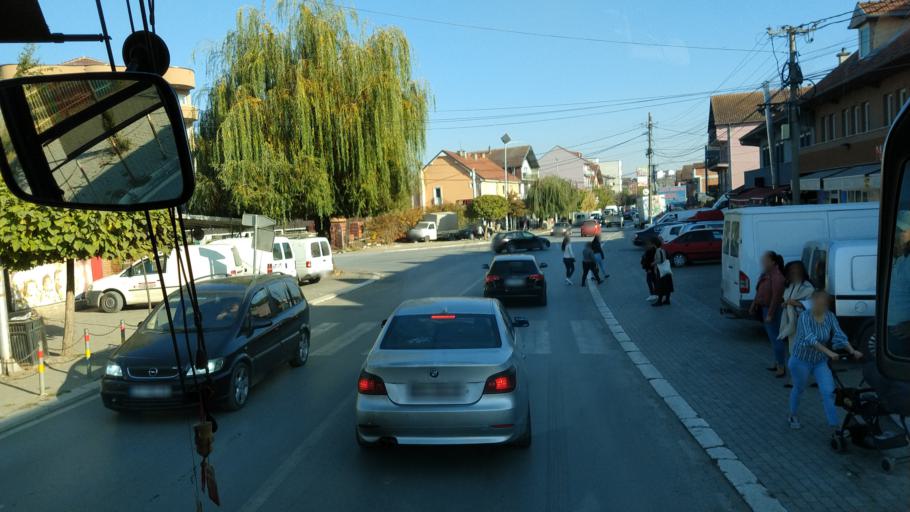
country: XK
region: Ferizaj
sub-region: Komuna e Shtimes
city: Shtime
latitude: 42.4355
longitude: 21.0325
